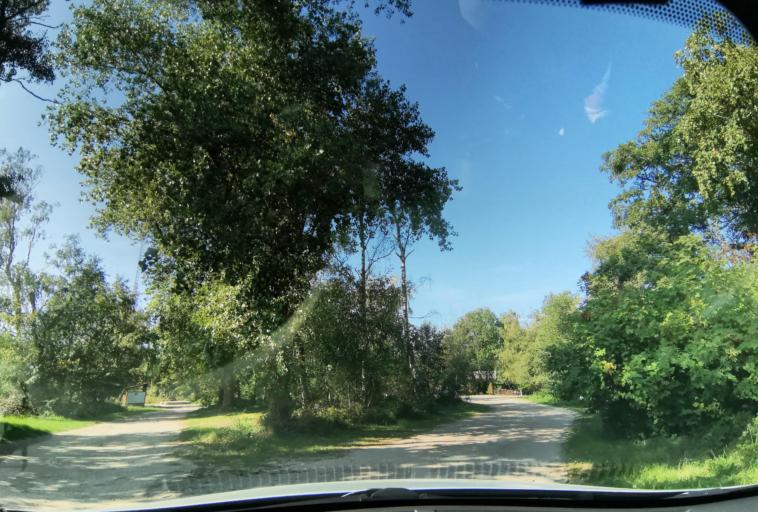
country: LT
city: Nida
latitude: 55.1634
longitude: 20.8189
